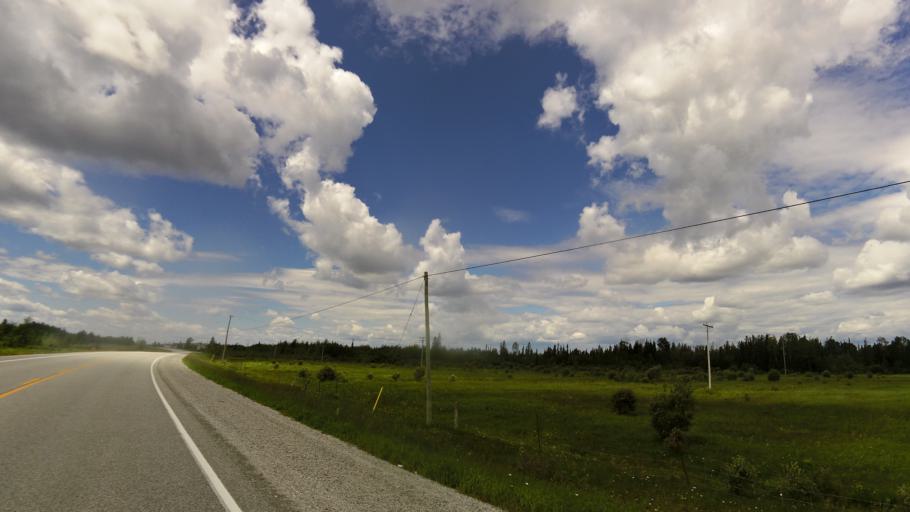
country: CA
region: Ontario
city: Kapuskasing
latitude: 49.2876
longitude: -81.8469
